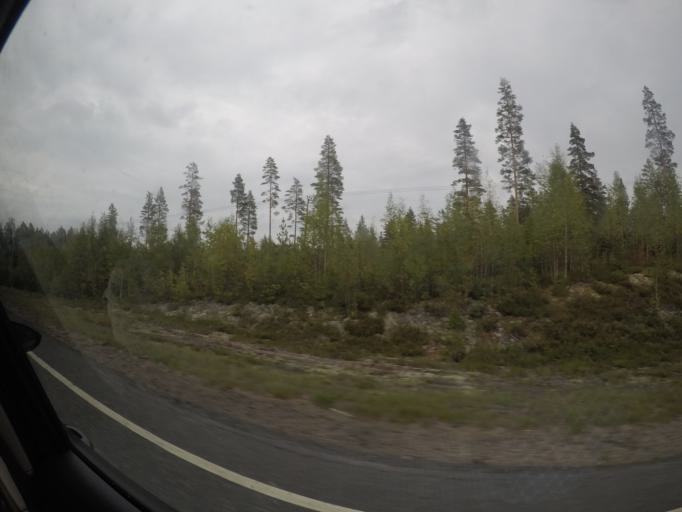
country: FI
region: Pirkanmaa
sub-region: Ylae-Pirkanmaa
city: Juupajoki
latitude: 61.8058
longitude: 24.2979
